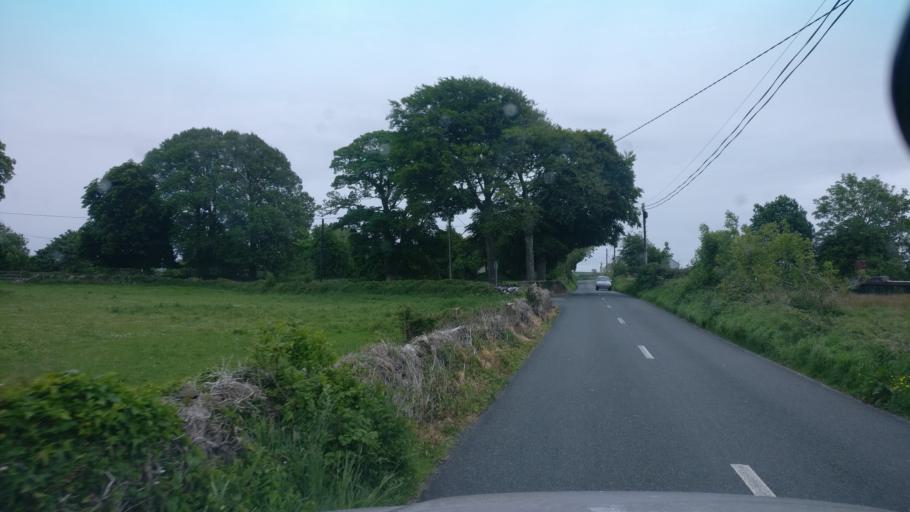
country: IE
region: Connaught
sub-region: County Galway
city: Gort
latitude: 53.0665
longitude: -8.7773
